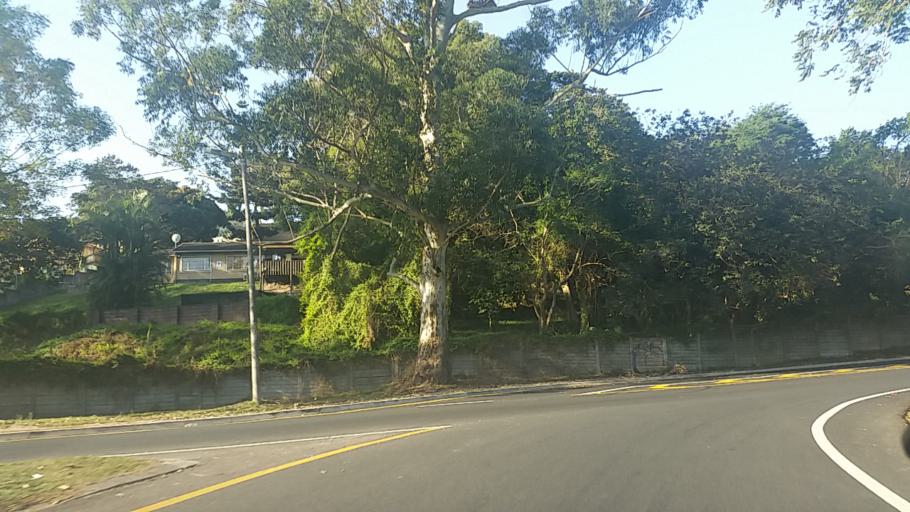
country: ZA
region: KwaZulu-Natal
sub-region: eThekwini Metropolitan Municipality
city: Berea
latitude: -29.8264
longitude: 30.8783
